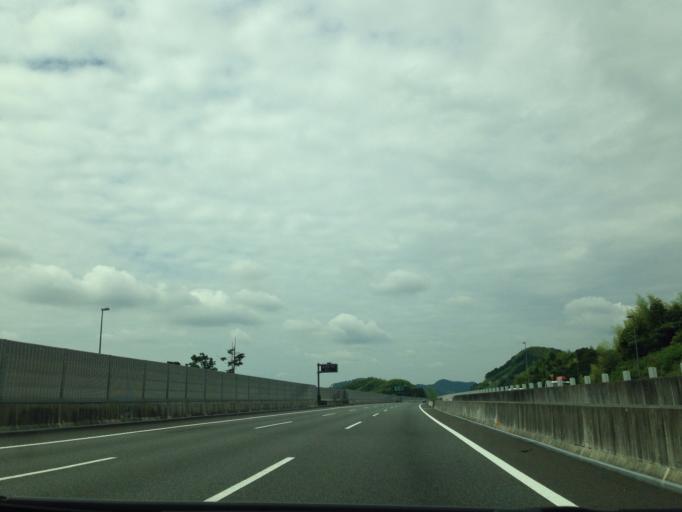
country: JP
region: Shizuoka
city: Fujieda
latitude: 34.9199
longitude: 138.2667
